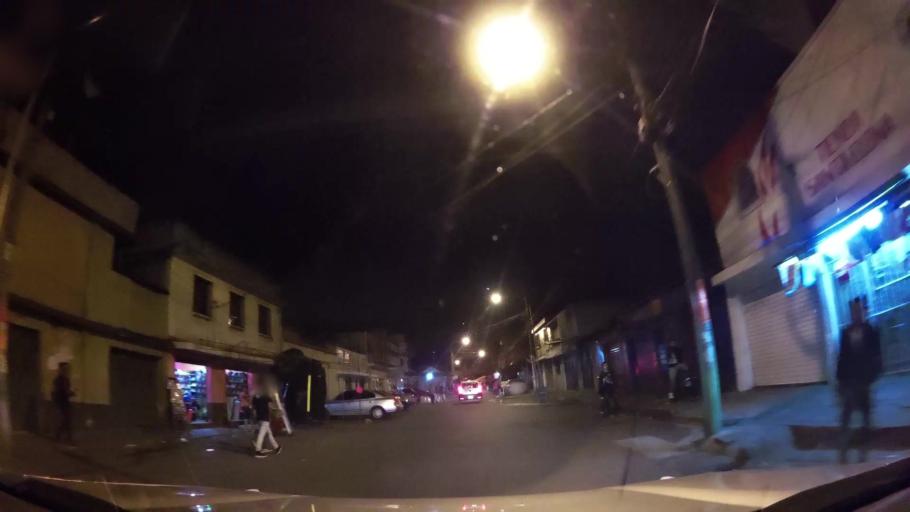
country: GT
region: Guatemala
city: Guatemala City
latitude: 14.6488
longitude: -90.4965
